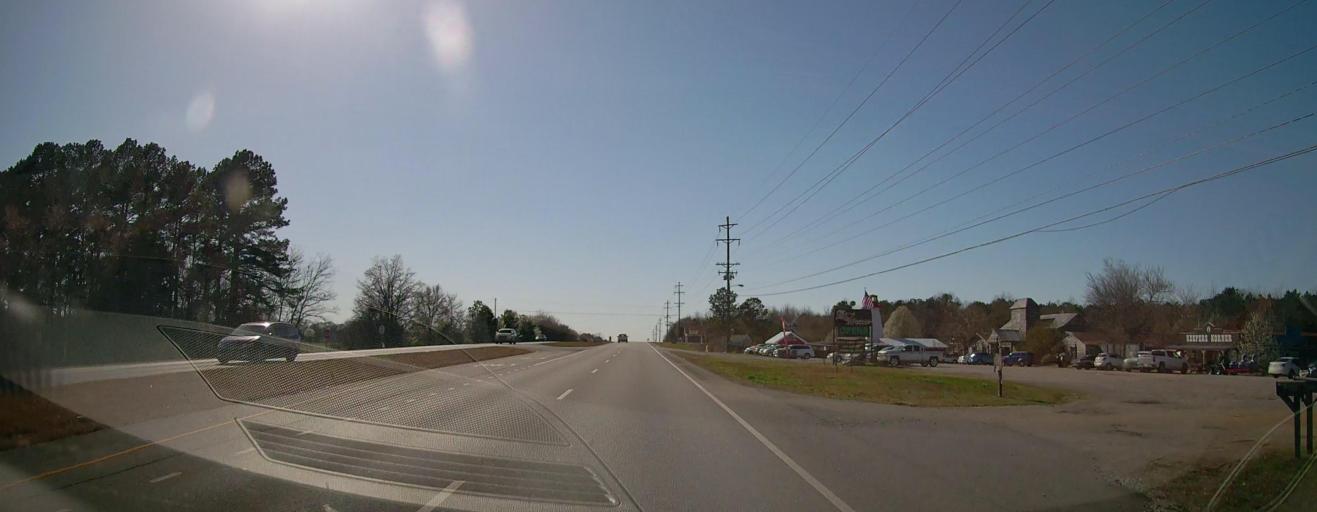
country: US
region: Alabama
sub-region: Lauderdale County
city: Killen
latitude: 34.8598
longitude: -87.4973
